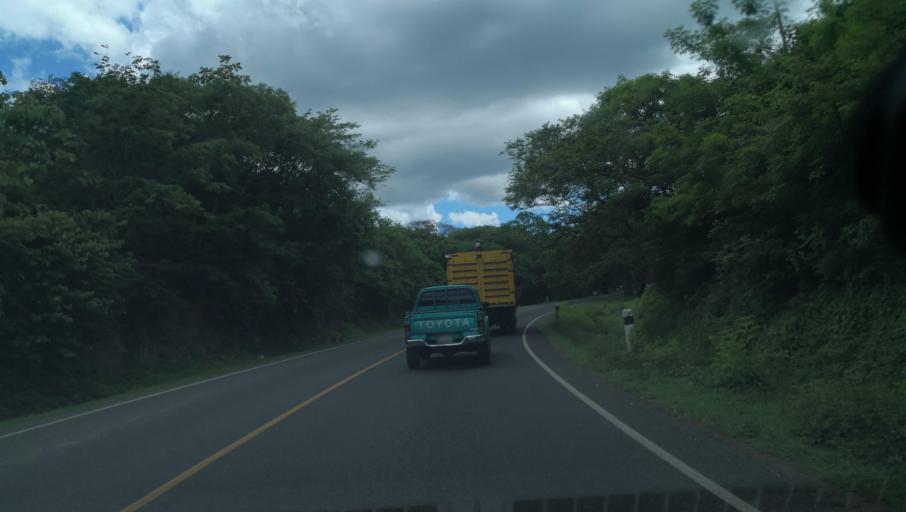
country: NI
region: Madriz
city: Yalaguina
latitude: 13.4577
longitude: -86.4596
